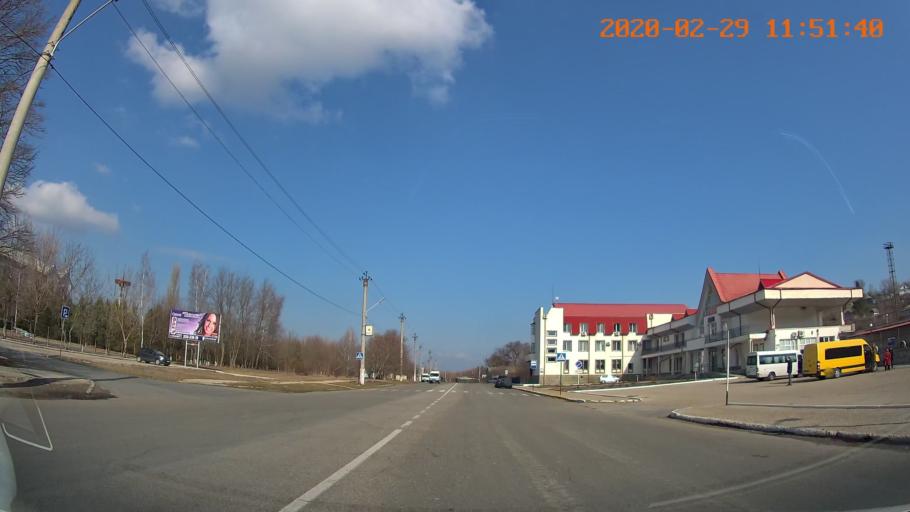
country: MD
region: Telenesti
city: Ribnita
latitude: 47.7658
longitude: 28.9904
